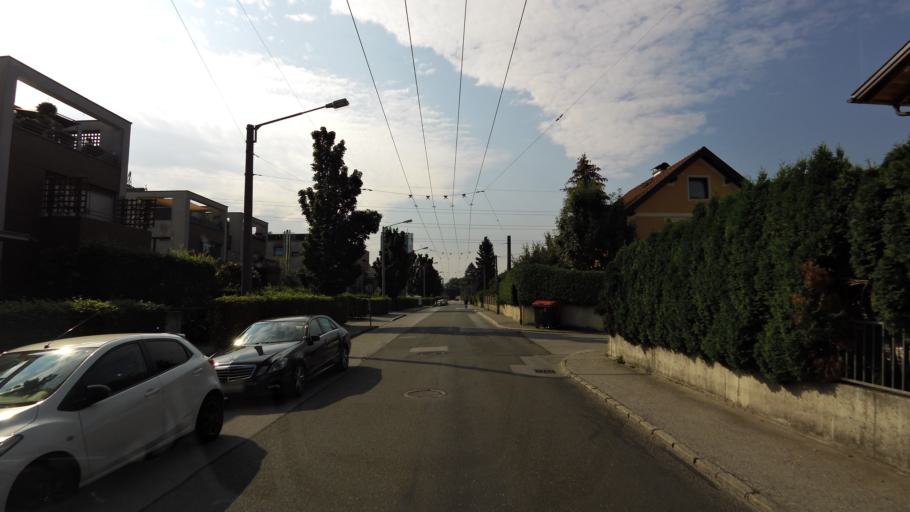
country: AT
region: Salzburg
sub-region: Politischer Bezirk Salzburg-Umgebung
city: Bergheim
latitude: 47.8304
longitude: 13.0220
